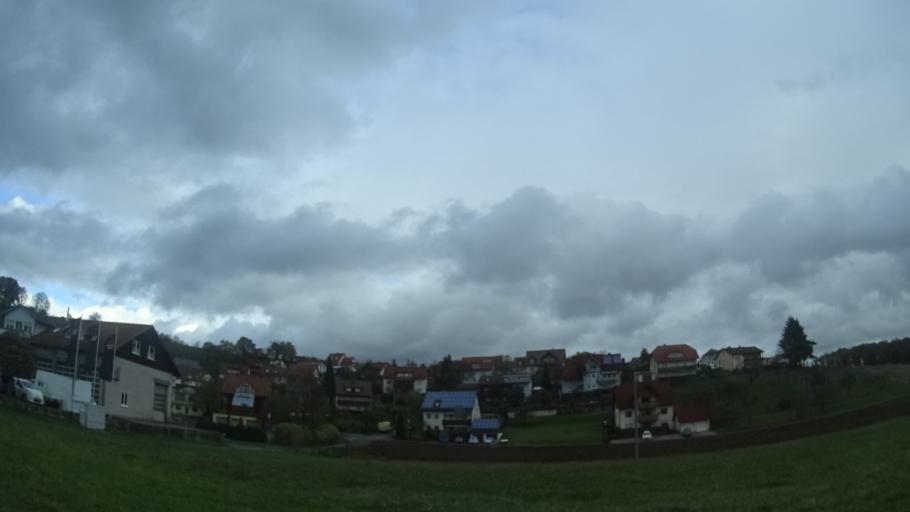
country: DE
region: Bavaria
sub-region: Regierungsbezirk Unterfranken
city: Hohenroth
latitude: 50.3348
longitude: 10.1447
